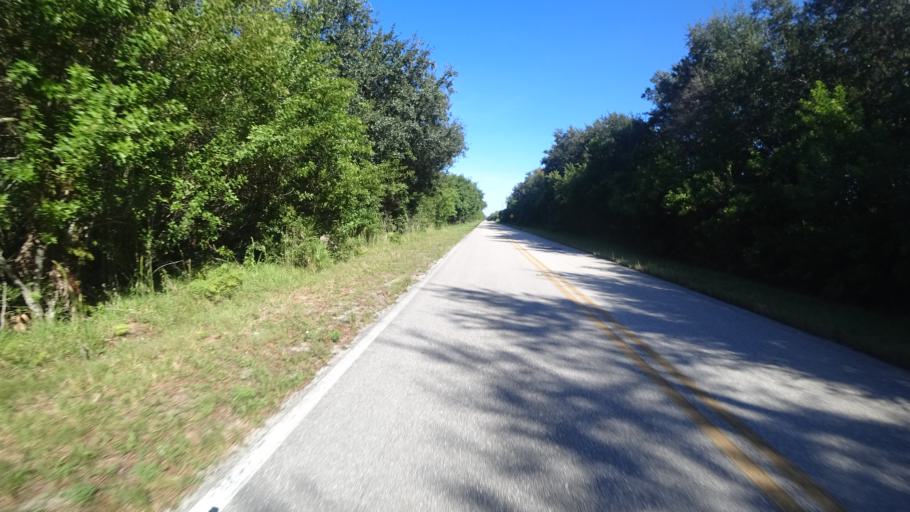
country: US
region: Florida
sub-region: Hillsborough County
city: Wimauma
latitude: 27.6281
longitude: -82.2925
